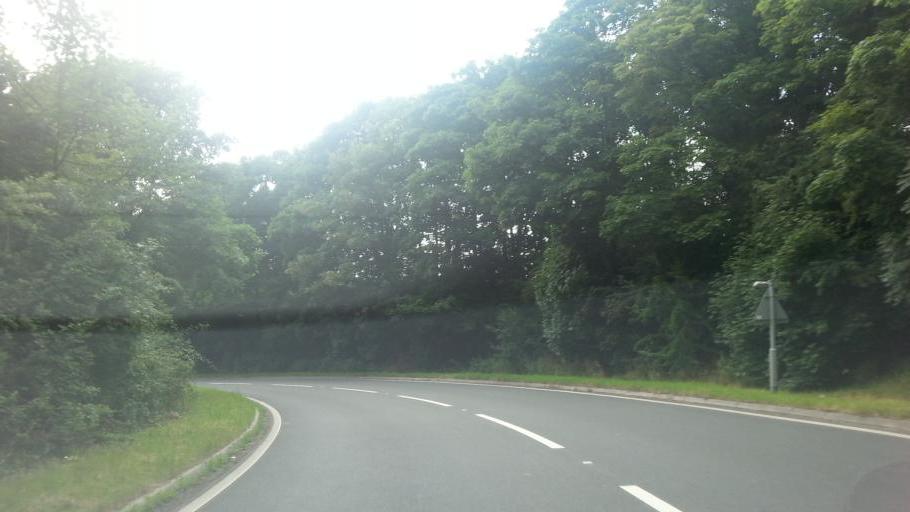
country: GB
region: England
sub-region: Nottinghamshire
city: Newark on Trent
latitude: 53.0795
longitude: -0.7695
